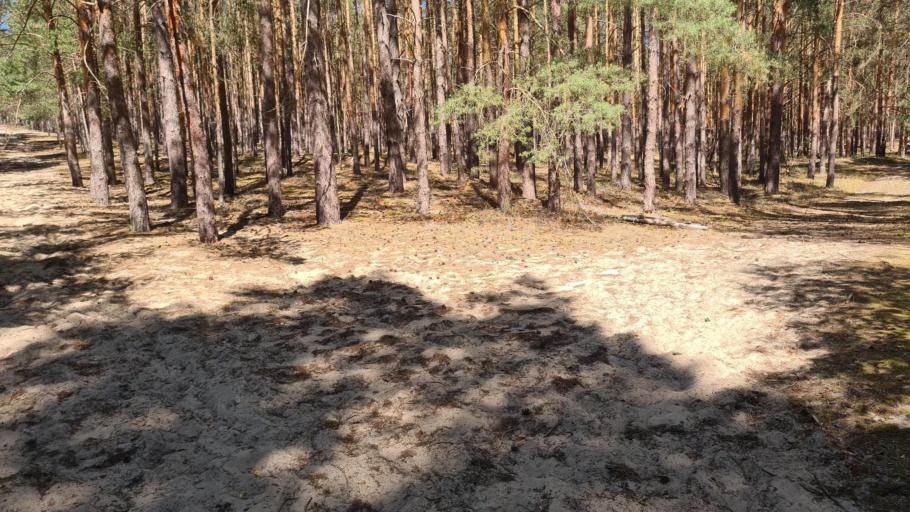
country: DE
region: Brandenburg
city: Trebbin
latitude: 52.2454
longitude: 13.1682
